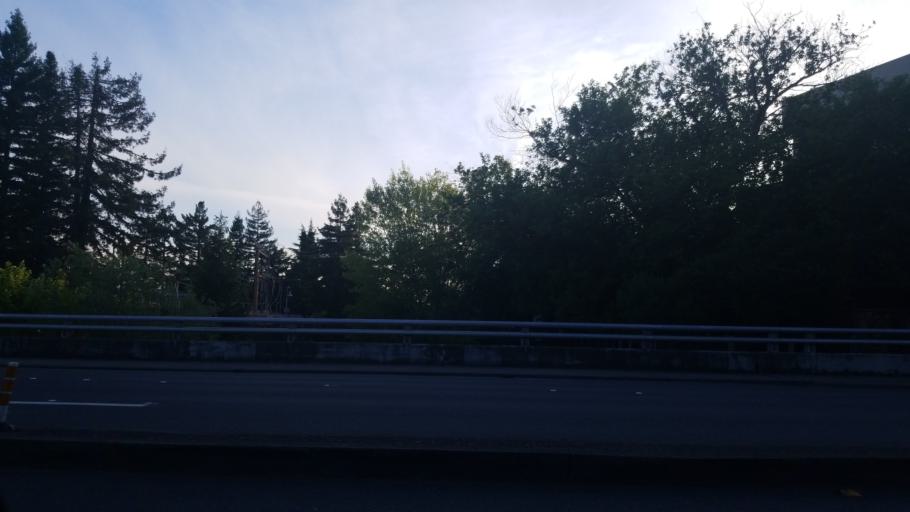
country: US
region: California
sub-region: Sonoma County
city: Santa Rosa
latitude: 38.4374
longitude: -122.7123
